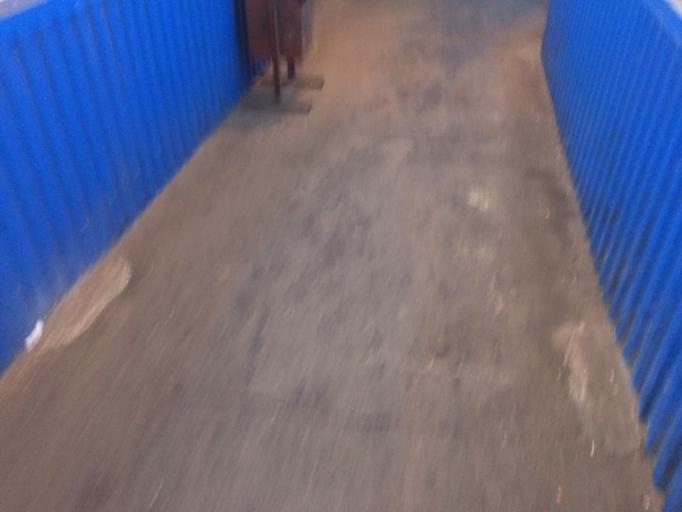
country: RU
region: Chelyabinsk
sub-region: Gorod Magnitogorsk
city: Magnitogorsk
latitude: 53.4034
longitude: 59.0450
